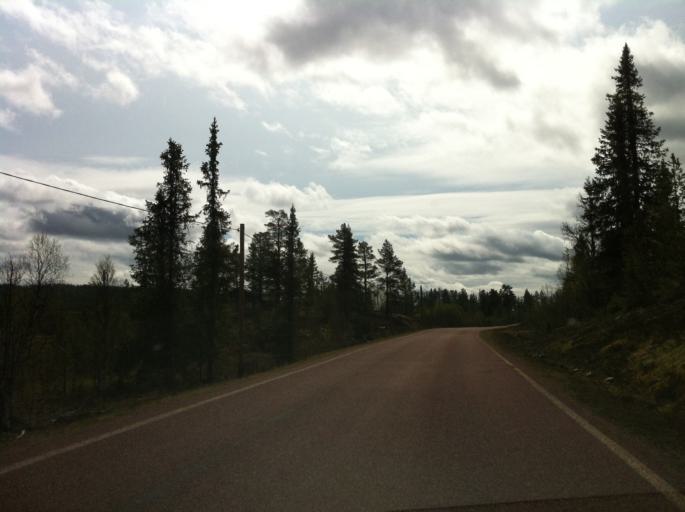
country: NO
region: Hedmark
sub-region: Engerdal
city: Engerdal
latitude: 62.1630
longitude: 12.9435
